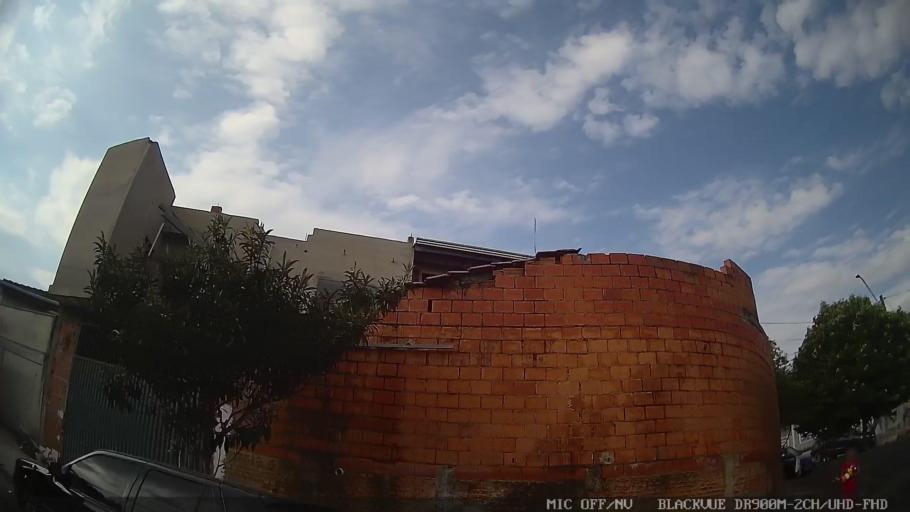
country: BR
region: Sao Paulo
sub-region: Indaiatuba
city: Indaiatuba
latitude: -23.0999
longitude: -47.2431
